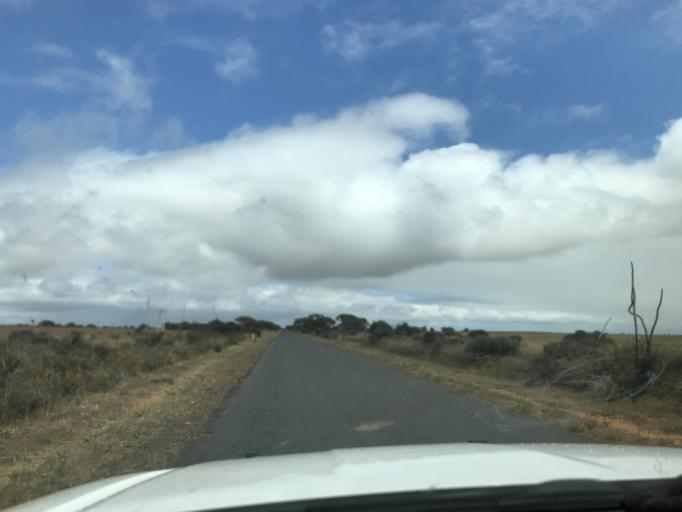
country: AU
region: South Australia
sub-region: Tatiara
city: Bordertown
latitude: -36.1377
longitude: 141.2040
